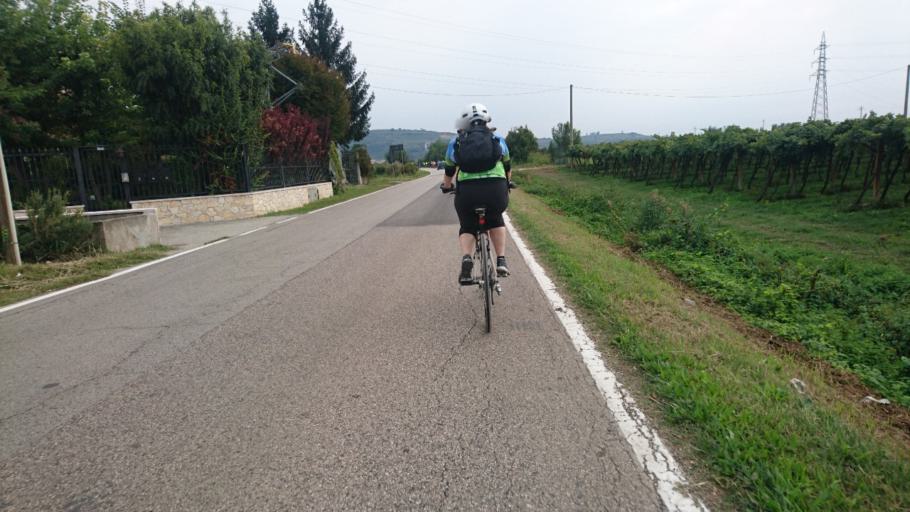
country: IT
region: Veneto
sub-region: Provincia di Verona
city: Soave
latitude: 45.4277
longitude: 11.2268
